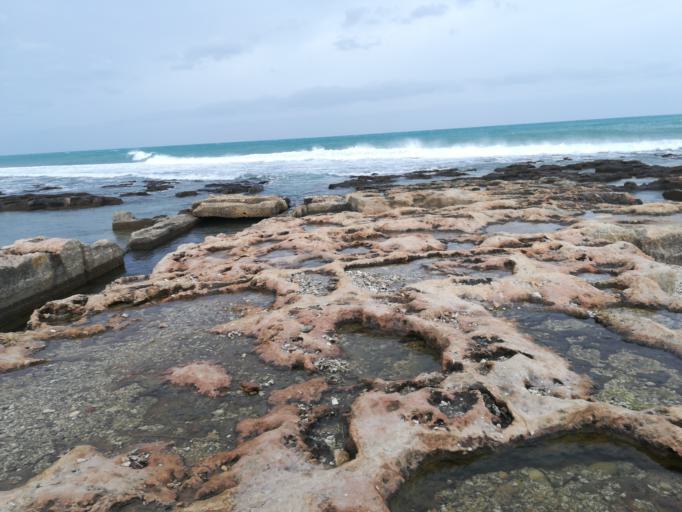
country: IT
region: Apulia
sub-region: Provincia di Bari
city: Polignano a Mare
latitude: 41.0154
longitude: 17.1917
